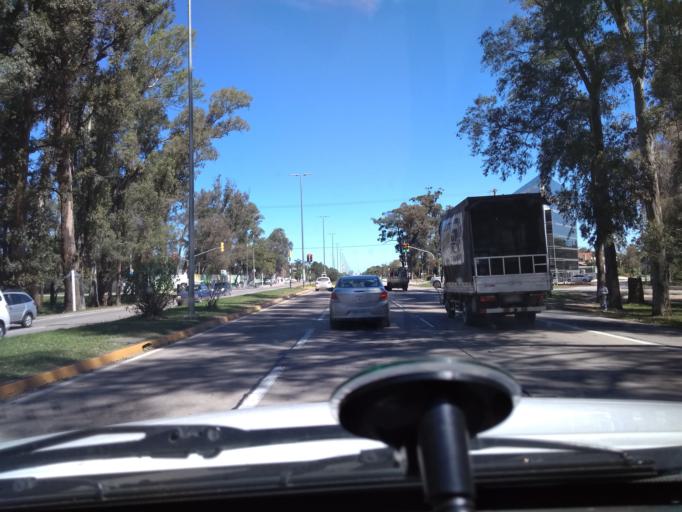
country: UY
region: Canelones
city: Barra de Carrasco
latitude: -34.8588
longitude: -56.0299
